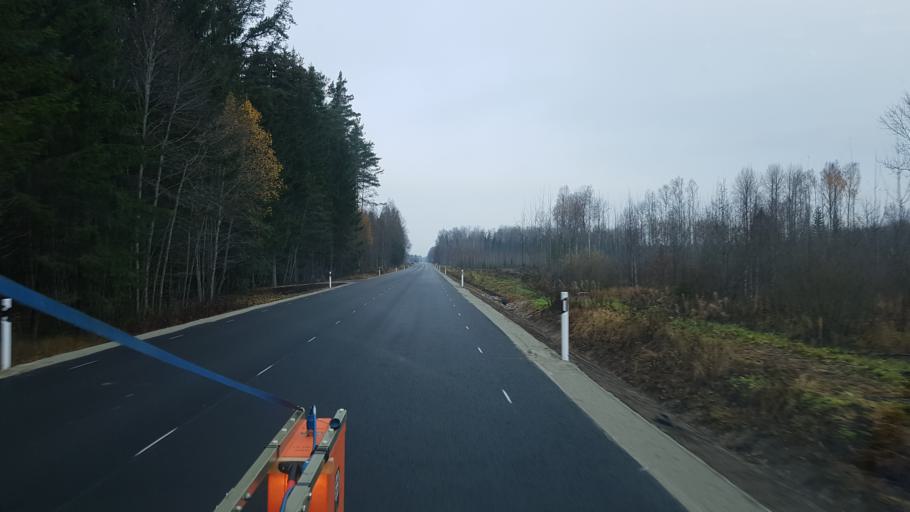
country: EE
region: Paernumaa
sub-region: Vaendra vald (alev)
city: Vandra
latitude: 58.8327
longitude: 25.0953
